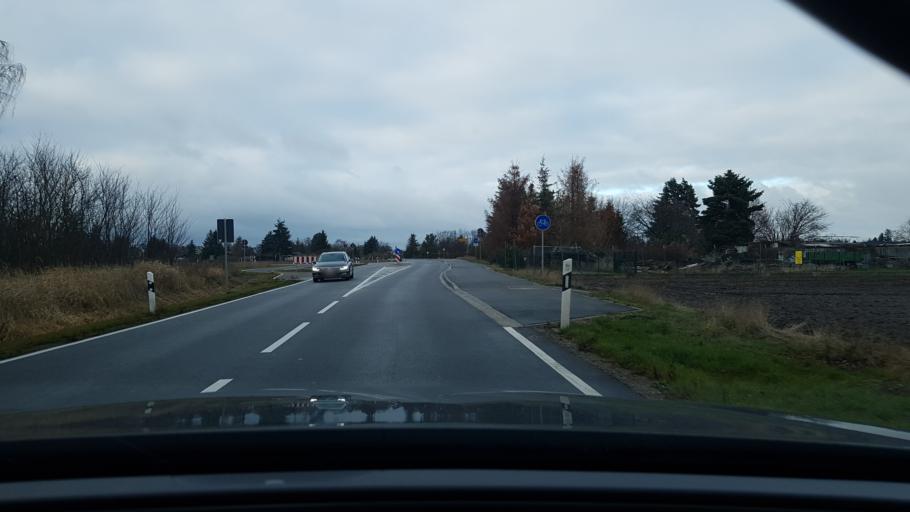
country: DE
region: Saxony-Anhalt
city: Oebisfelde
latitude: 52.4236
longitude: 11.0020
